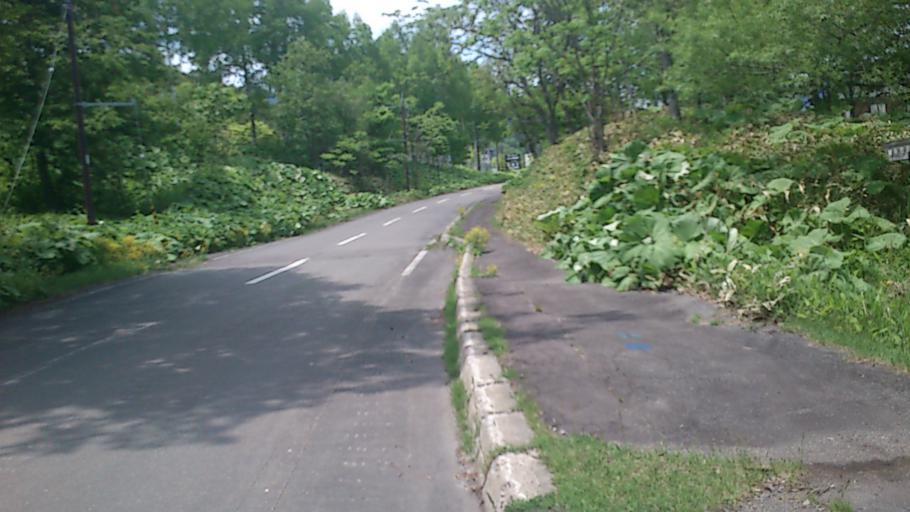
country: JP
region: Hokkaido
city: Otofuke
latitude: 43.3652
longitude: 143.1949
